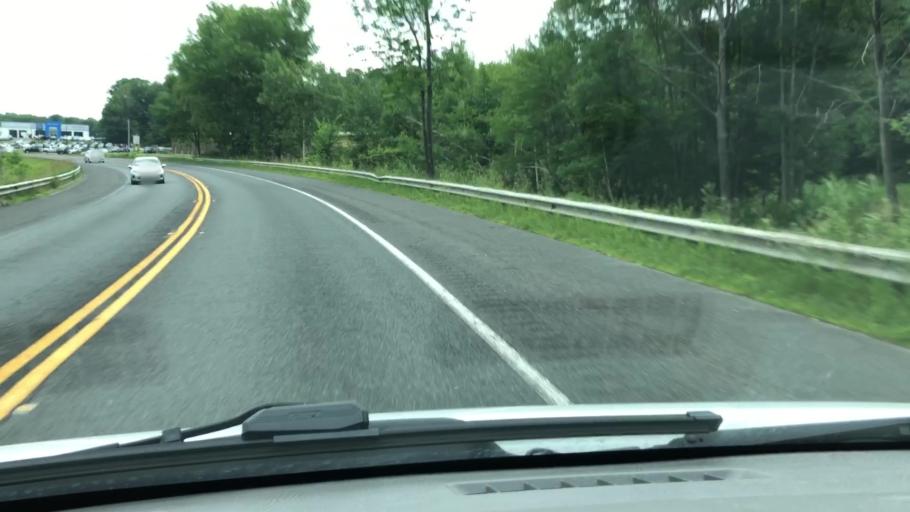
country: US
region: Massachusetts
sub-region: Berkshire County
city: Lanesborough
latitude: 42.5478
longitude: -73.1658
